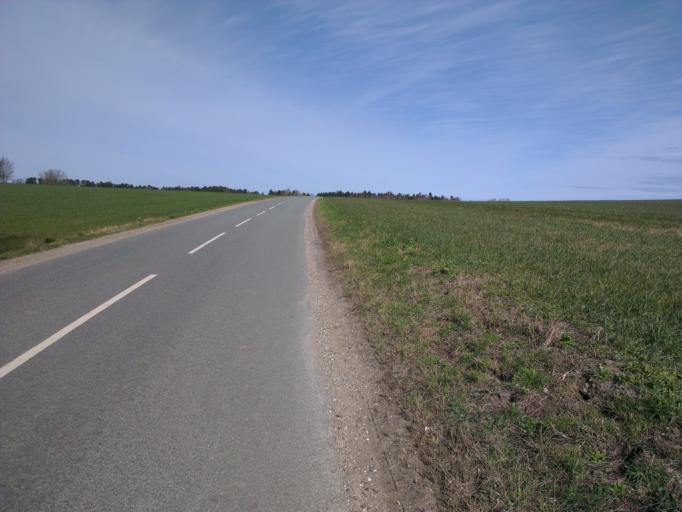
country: DK
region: Capital Region
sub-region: Frederikssund Kommune
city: Frederikssund
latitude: 55.8440
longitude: 12.1254
